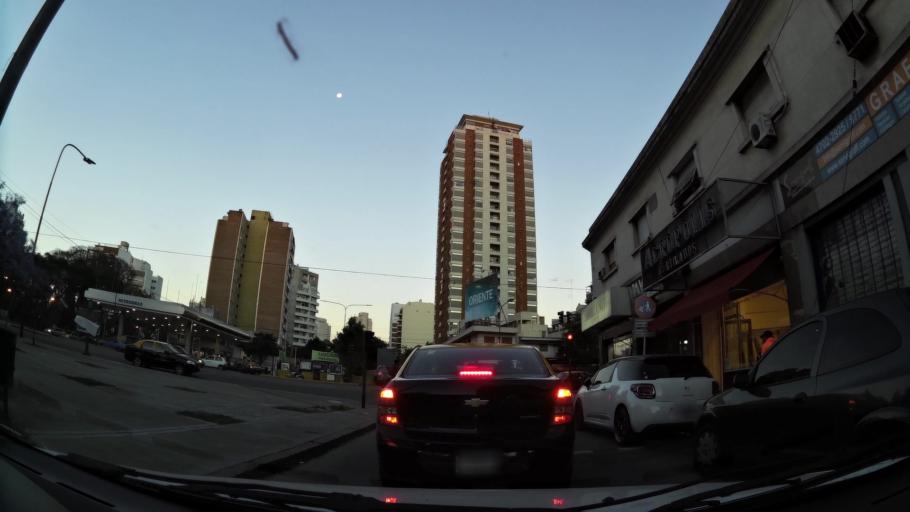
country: AR
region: Buenos Aires F.D.
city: Colegiales
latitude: -34.5487
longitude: -58.4689
